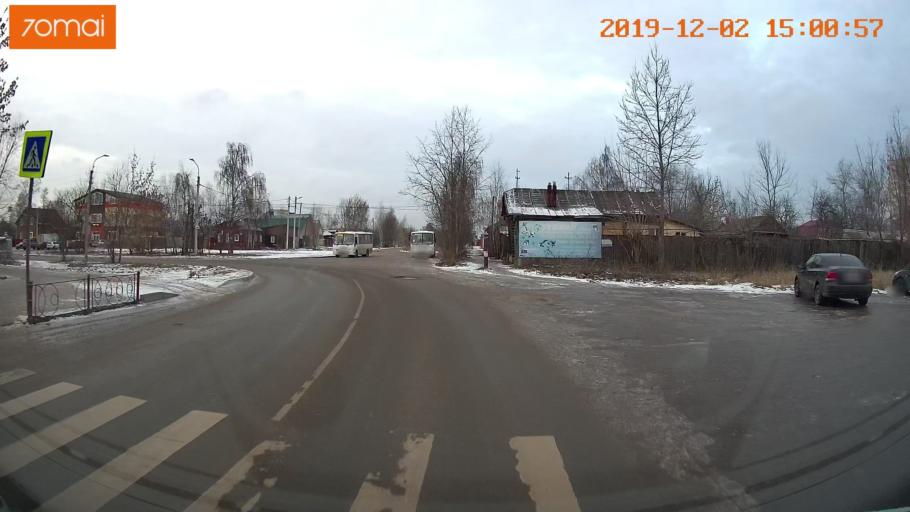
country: RU
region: Ivanovo
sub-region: Gorod Ivanovo
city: Ivanovo
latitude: 56.9731
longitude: 41.0010
